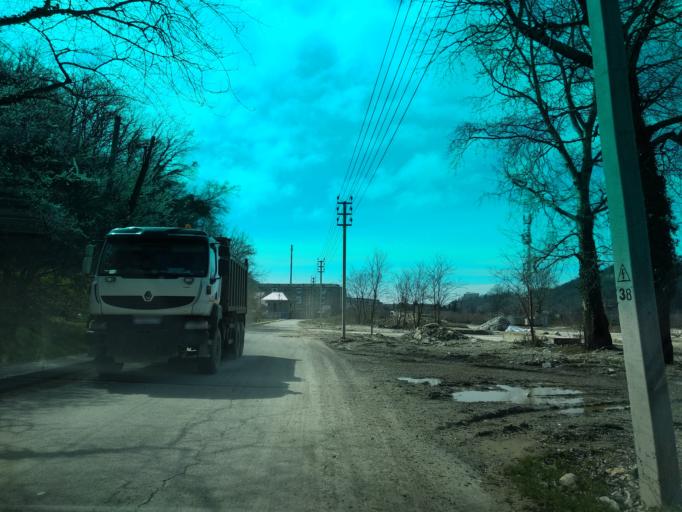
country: RU
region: Krasnodarskiy
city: Shepsi
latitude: 44.0462
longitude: 39.1569
